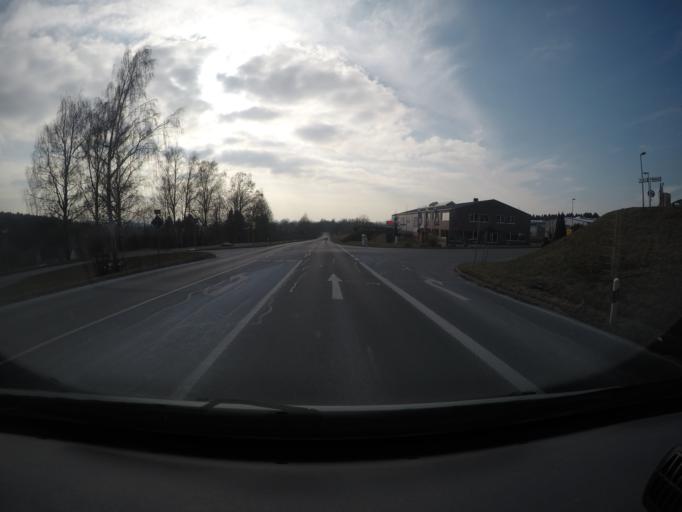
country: DE
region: Saxony
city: Oederan
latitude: 50.8686
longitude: 13.1896
